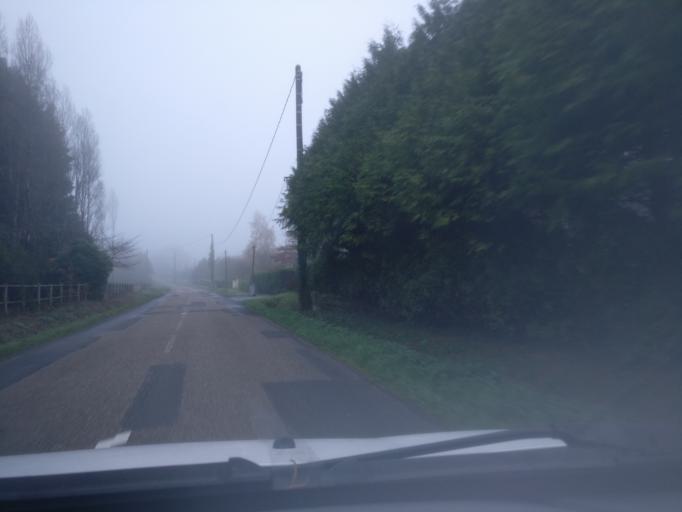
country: FR
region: Brittany
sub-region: Departement d'Ille-et-Vilaine
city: Laille
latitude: 47.9920
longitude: -1.7156
